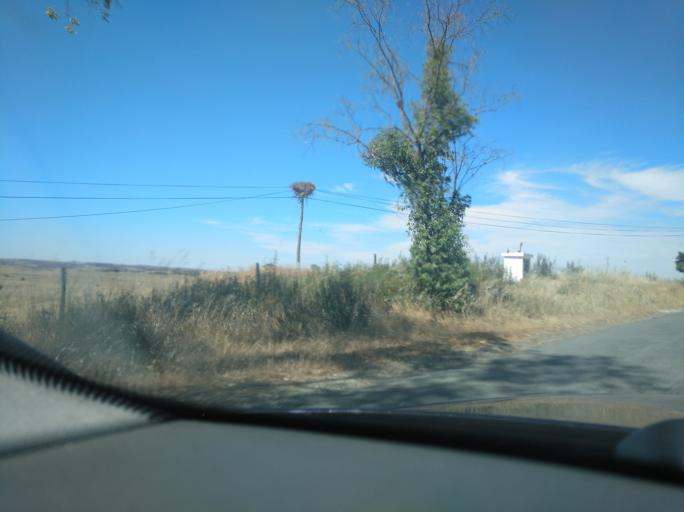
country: PT
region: Beja
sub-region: Almodovar
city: Almodovar
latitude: 37.5409
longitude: -7.9651
